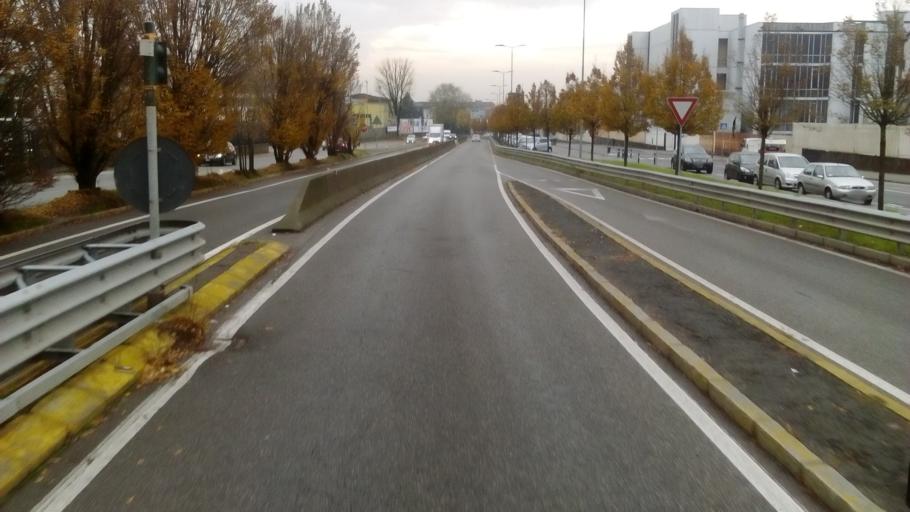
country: IT
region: Lombardy
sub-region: Provincia di Bergamo
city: Torre Boldone
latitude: 45.7111
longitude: 9.6881
